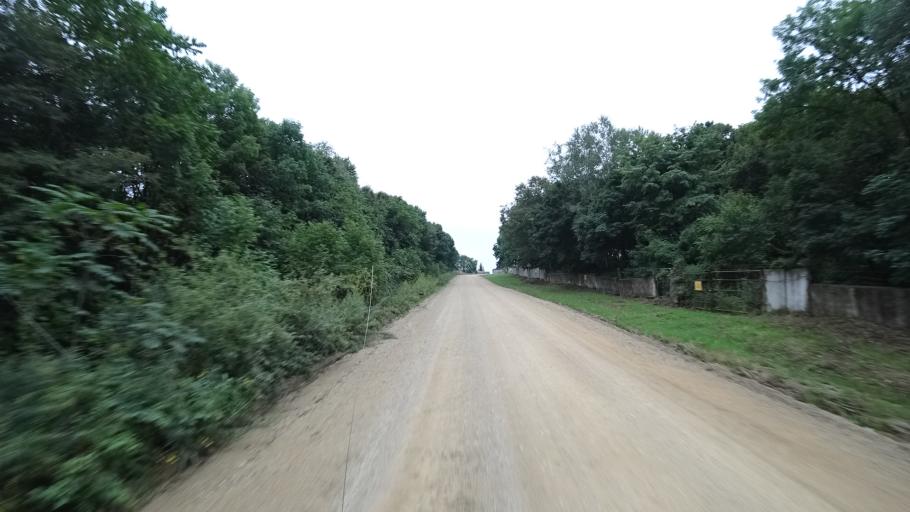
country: RU
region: Primorskiy
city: Rettikhovka
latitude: 44.1769
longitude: 132.8519
